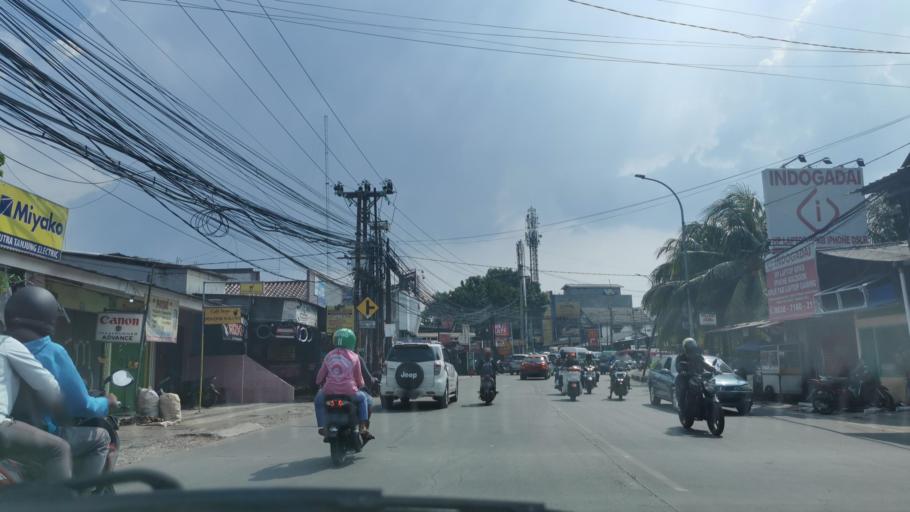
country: ID
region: West Java
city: Depok
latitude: -6.4034
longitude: 106.8381
